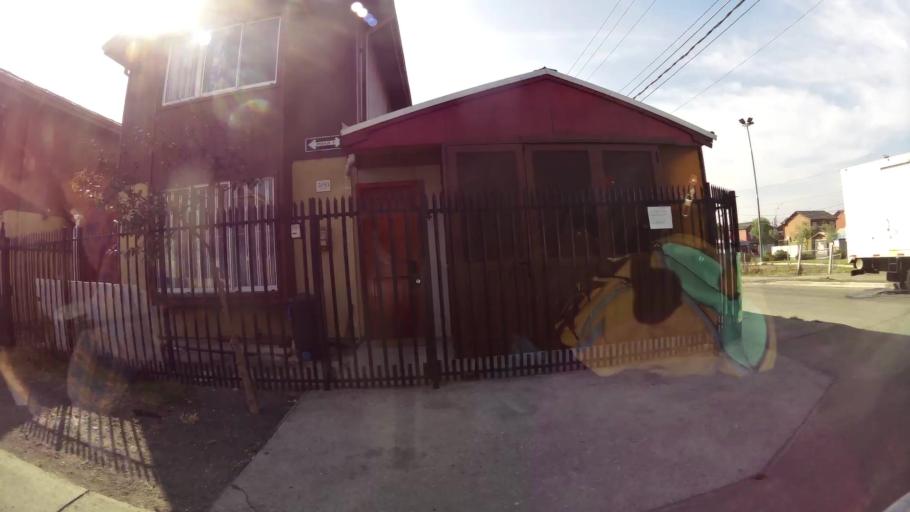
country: CL
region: Biobio
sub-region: Provincia de Concepcion
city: Talcahuano
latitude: -36.7933
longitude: -73.1151
